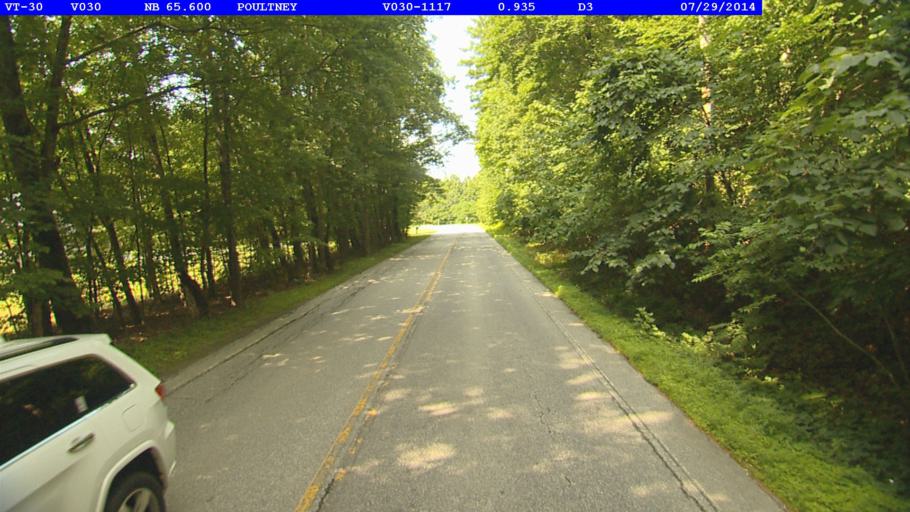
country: US
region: Vermont
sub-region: Rutland County
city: Poultney
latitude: 43.4772
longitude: -73.2014
